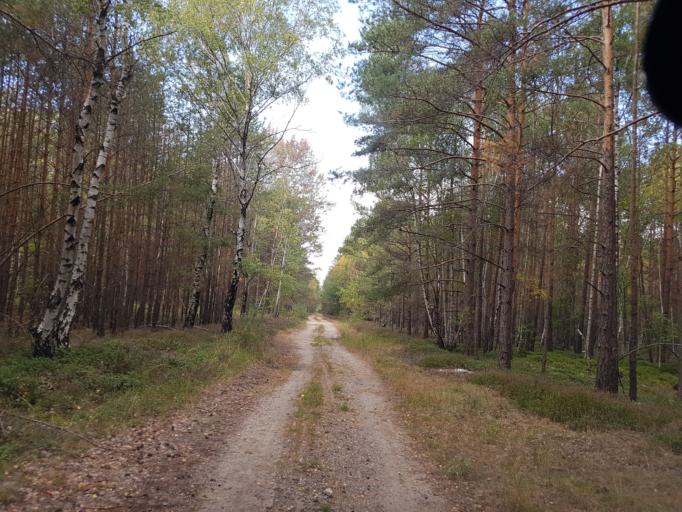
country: DE
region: Brandenburg
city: Finsterwalde
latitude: 51.5908
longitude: 13.7490
